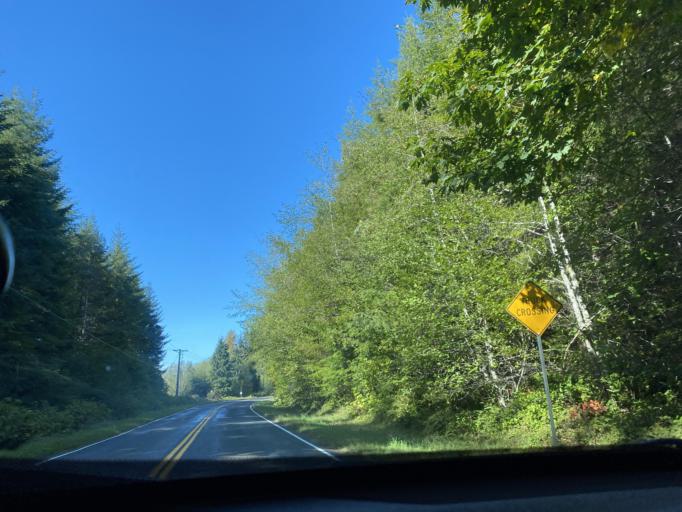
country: US
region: Washington
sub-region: Clallam County
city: Forks
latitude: 47.9471
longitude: -124.4963
